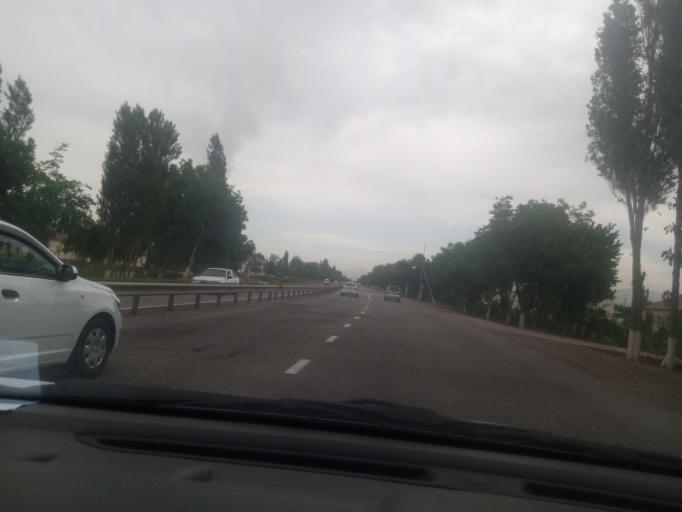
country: UZ
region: Toshkent
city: Ohangaron
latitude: 40.9080
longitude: 69.7703
